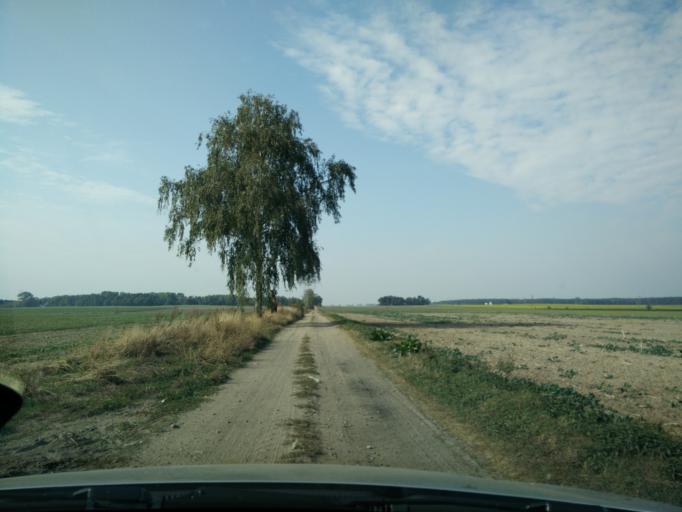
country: PL
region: Greater Poland Voivodeship
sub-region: Powiat sredzki
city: Sroda Wielkopolska
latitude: 52.3056
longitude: 17.2723
